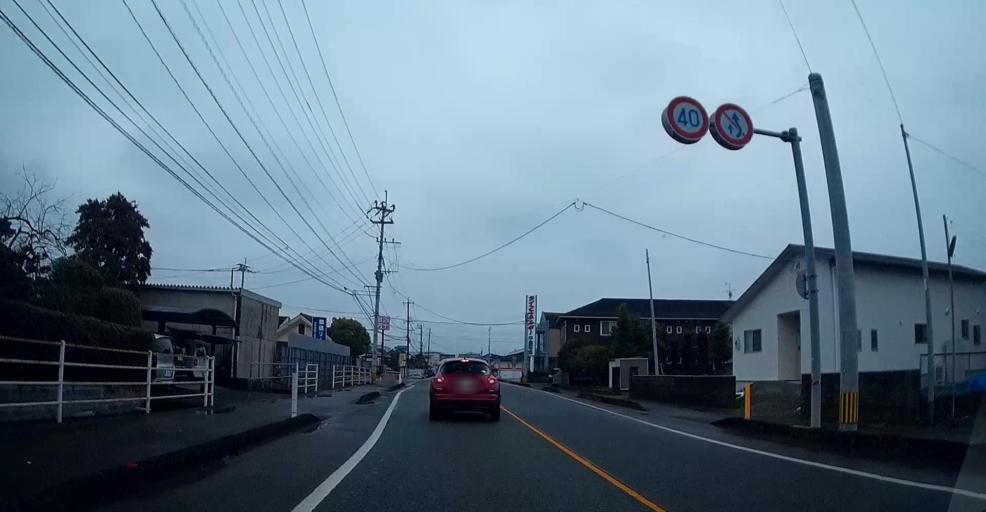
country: JP
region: Kumamoto
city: Kumamoto
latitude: 32.7463
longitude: 130.7387
